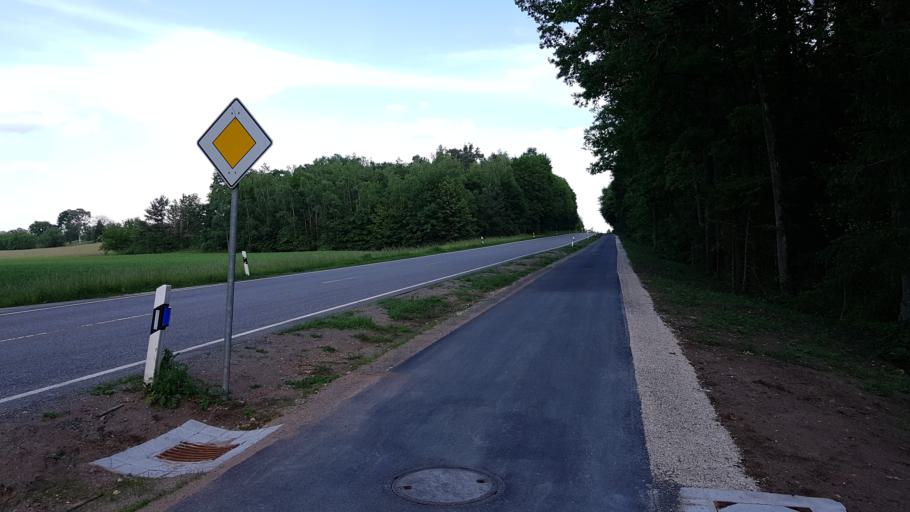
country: DE
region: Bavaria
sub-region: Regierungsbezirk Mittelfranken
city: Hilpoltstein
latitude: 49.1972
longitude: 11.1741
